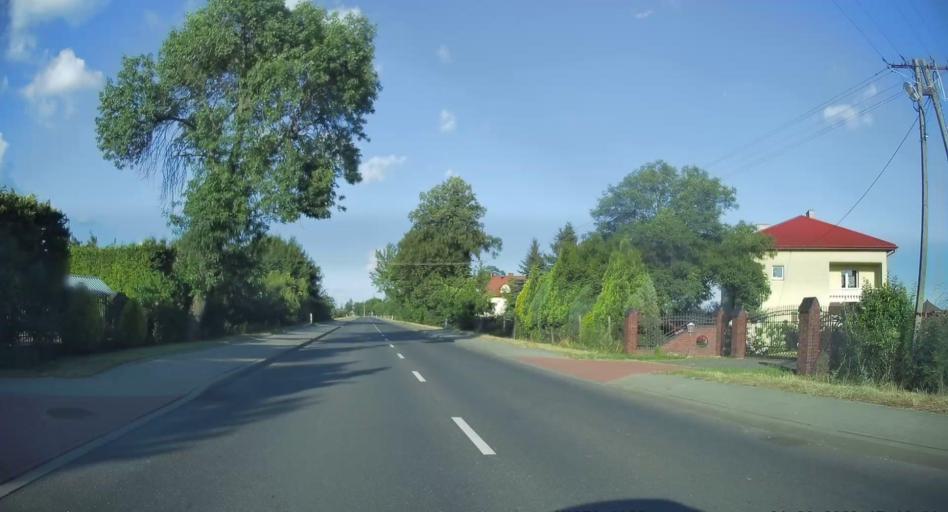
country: PL
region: Lodz Voivodeship
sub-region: Powiat rawski
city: Biala Rawska
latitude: 51.8043
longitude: 20.5534
